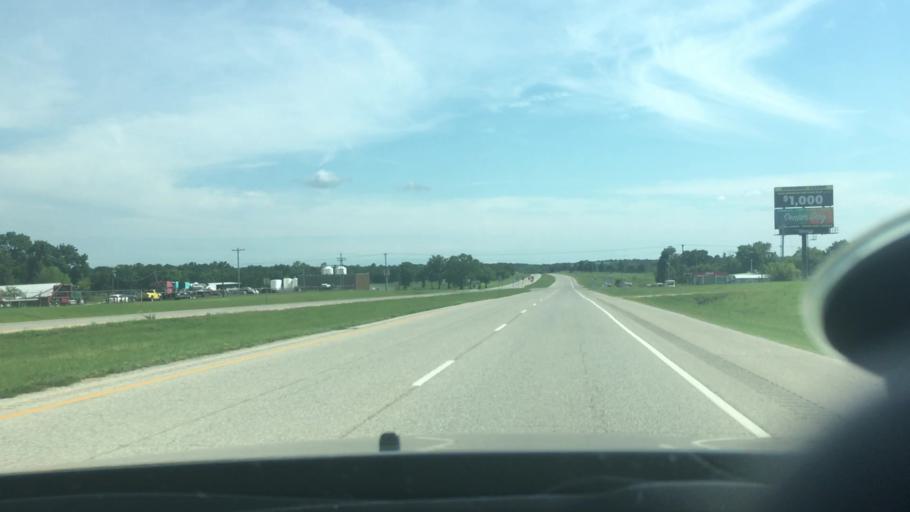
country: US
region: Oklahoma
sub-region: Seminole County
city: Seminole
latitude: 35.1909
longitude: -96.6752
